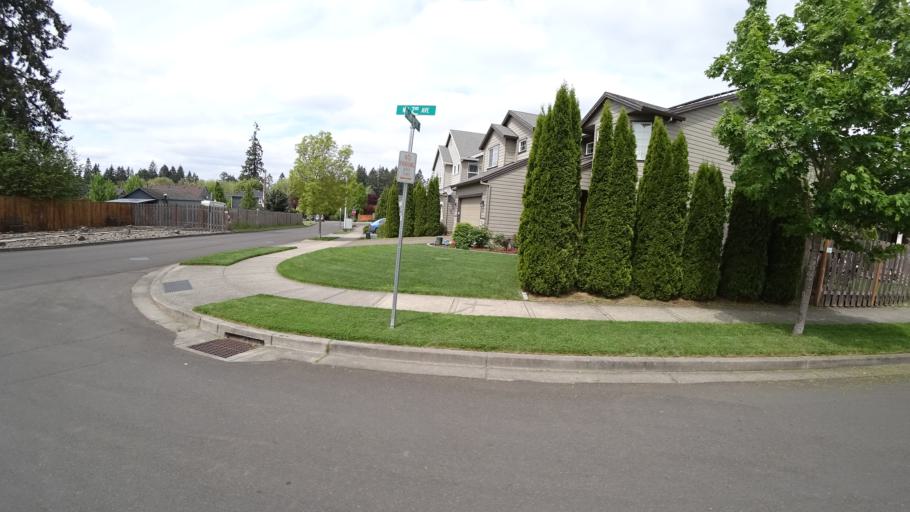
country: US
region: Oregon
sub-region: Washington County
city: Hillsboro
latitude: 45.5467
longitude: -122.9979
